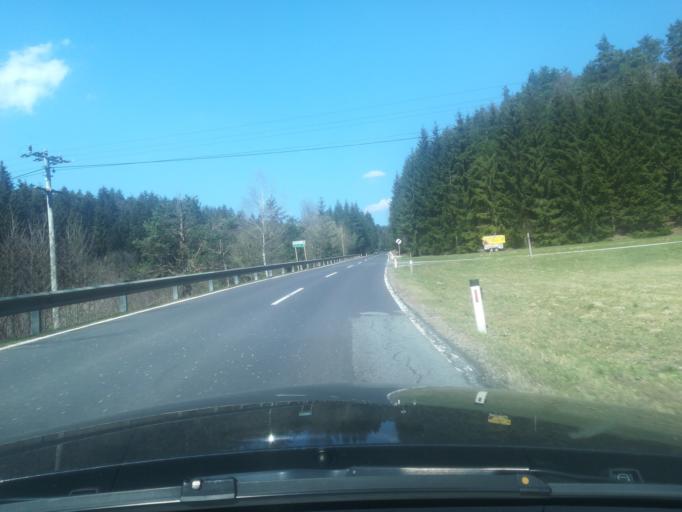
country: AT
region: Upper Austria
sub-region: Politischer Bezirk Perg
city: Bad Kreuzen
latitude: 48.4060
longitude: 14.7292
